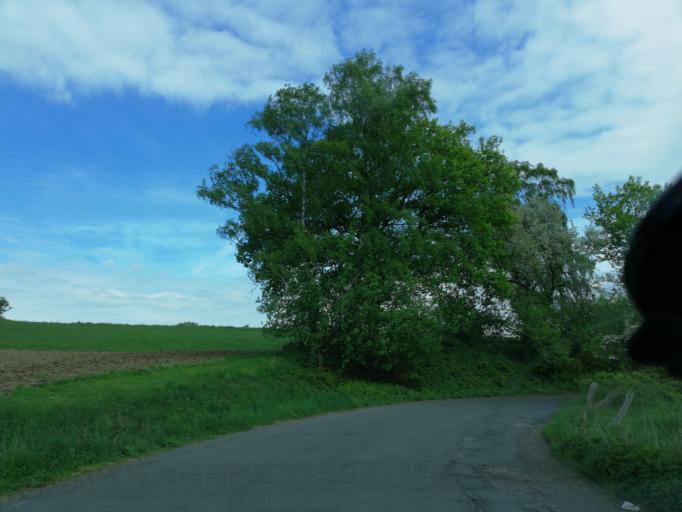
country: DE
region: North Rhine-Westphalia
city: Gevelsberg
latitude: 51.3634
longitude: 7.3051
